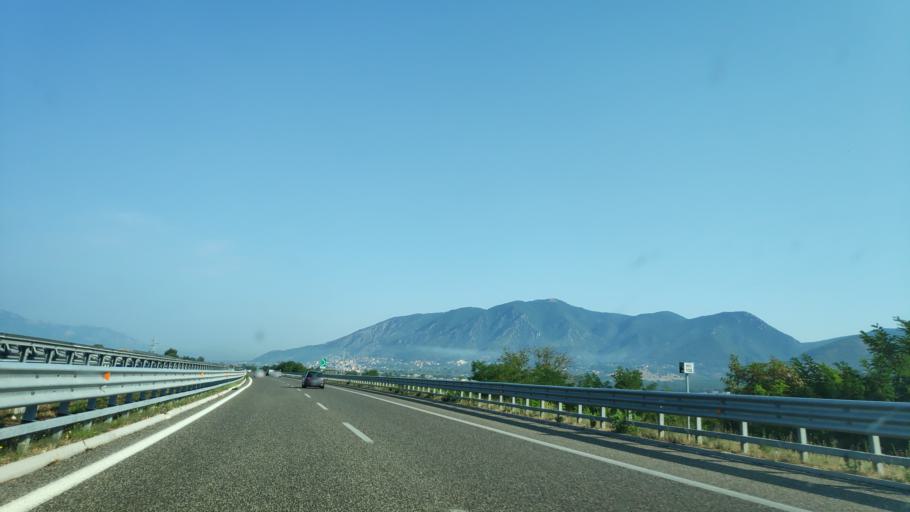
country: IT
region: Campania
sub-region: Provincia di Salerno
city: Padula
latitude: 40.3444
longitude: 15.6219
